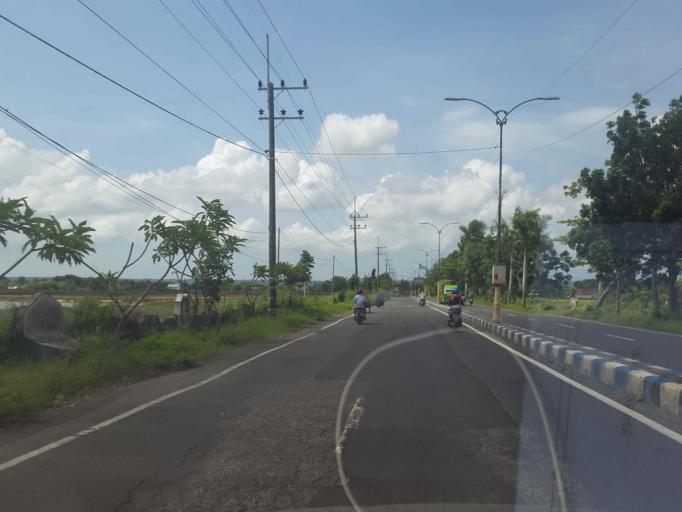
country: ID
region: East Java
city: Palebunan
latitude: -7.0472
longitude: 113.8452
